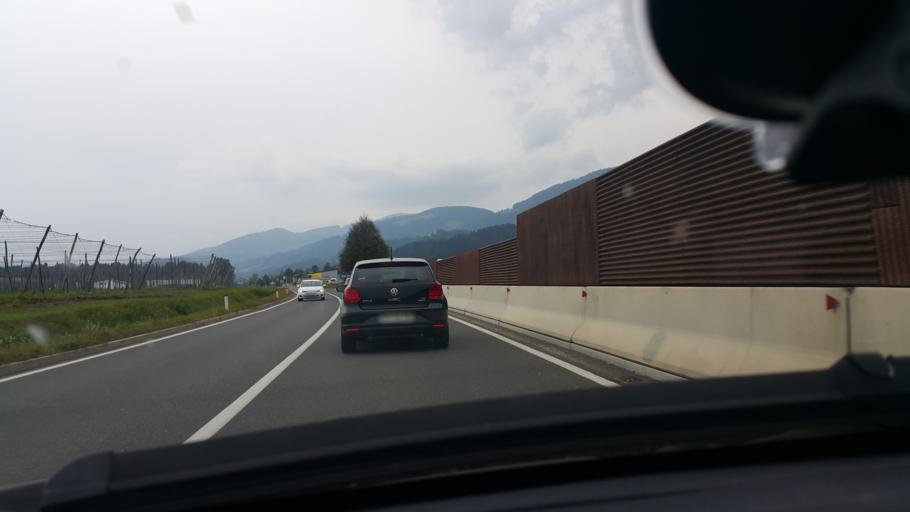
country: SI
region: Radlje ob Dravi
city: Radlje ob Dravi
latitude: 46.6137
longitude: 15.2148
